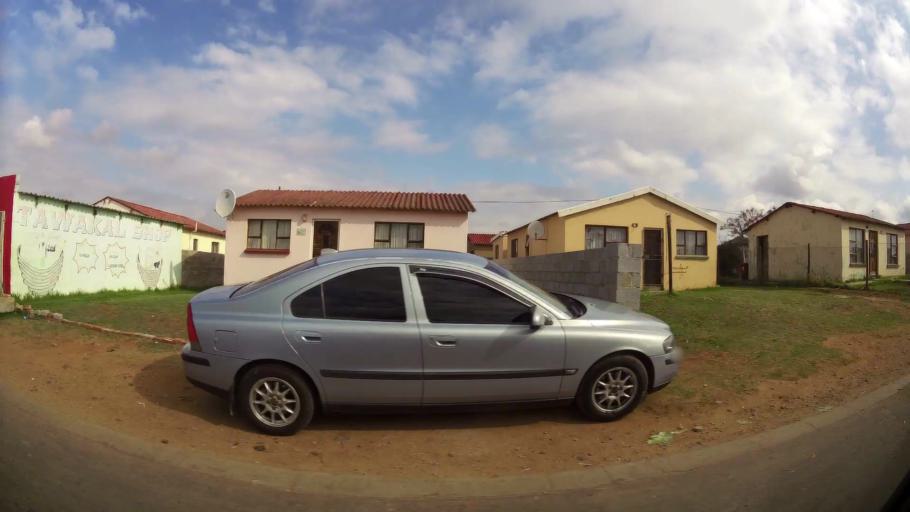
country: ZA
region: Eastern Cape
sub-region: Nelson Mandela Bay Metropolitan Municipality
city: Port Elizabeth
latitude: -33.8100
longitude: 25.5886
